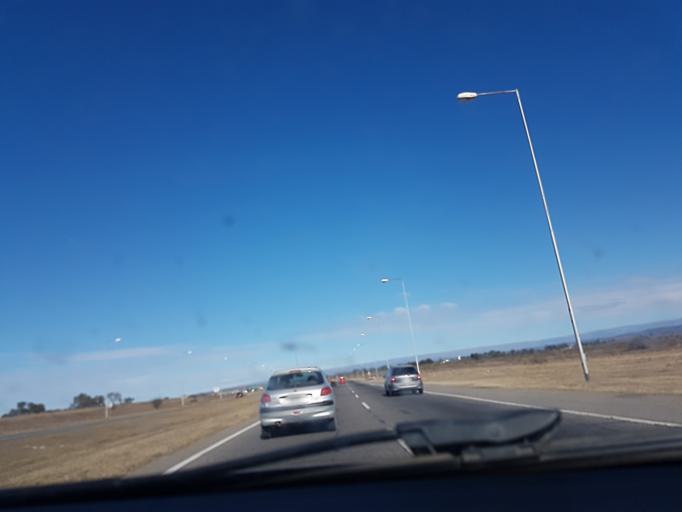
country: AR
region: Cordoba
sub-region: Departamento de Capital
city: Cordoba
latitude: -31.4214
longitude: -64.2727
